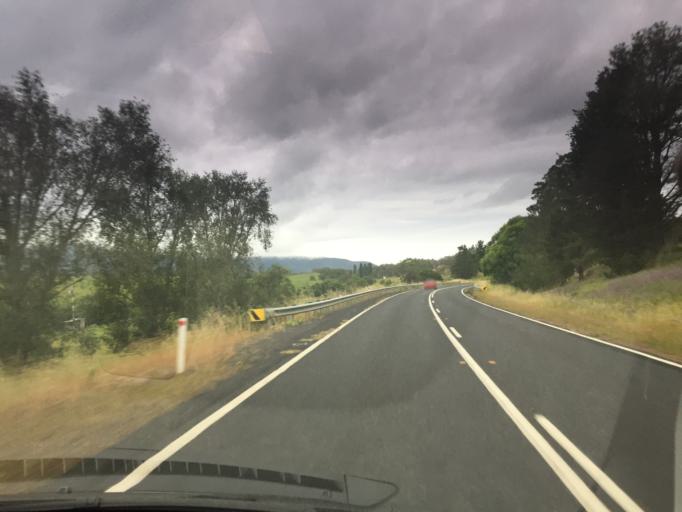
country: AU
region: New South Wales
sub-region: Bega Valley
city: Bega
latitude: -36.6160
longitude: 149.5521
